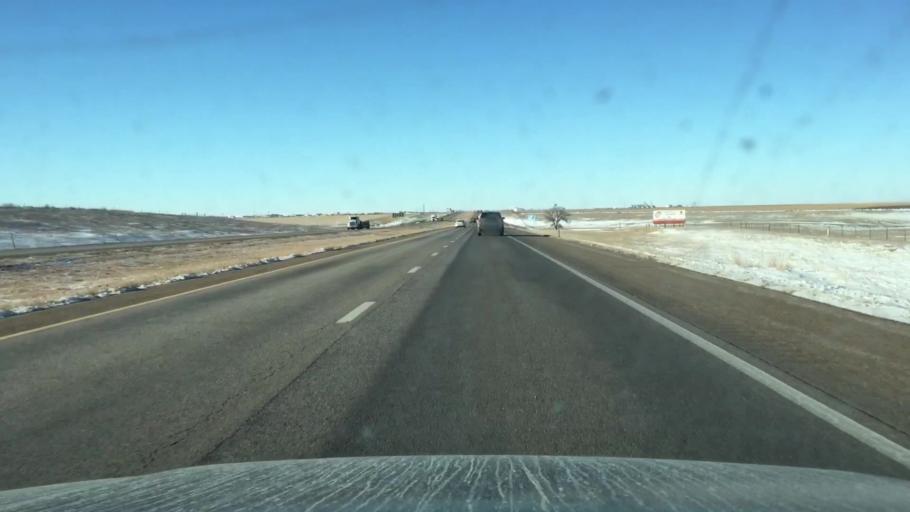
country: US
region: Kansas
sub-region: Thomas County
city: Colby
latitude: 39.3328
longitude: -101.0036
